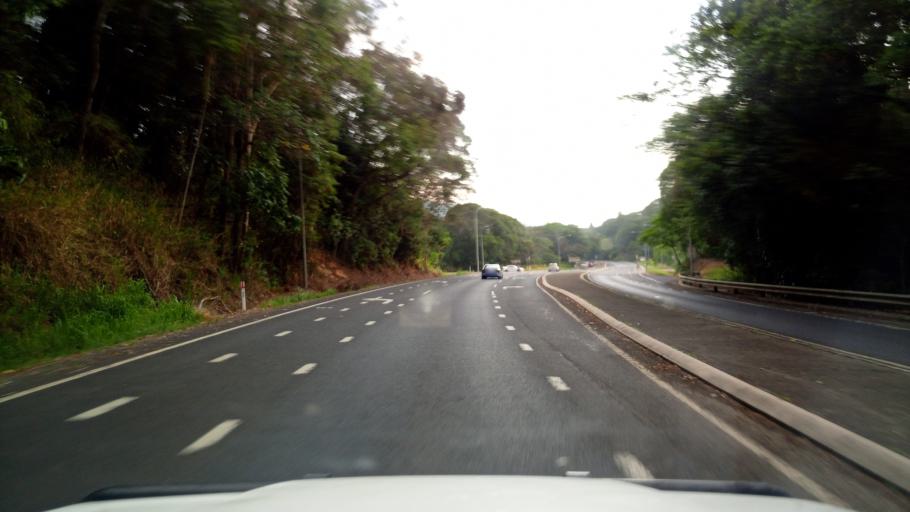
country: AU
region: Queensland
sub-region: Tablelands
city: Kuranda
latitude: -16.8308
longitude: 145.6213
